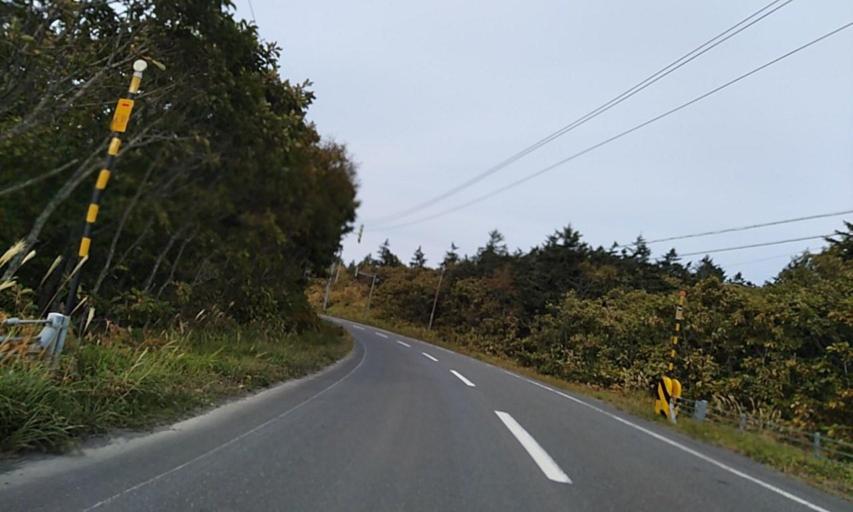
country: JP
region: Hokkaido
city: Makubetsu
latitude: 44.9980
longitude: 141.6960
